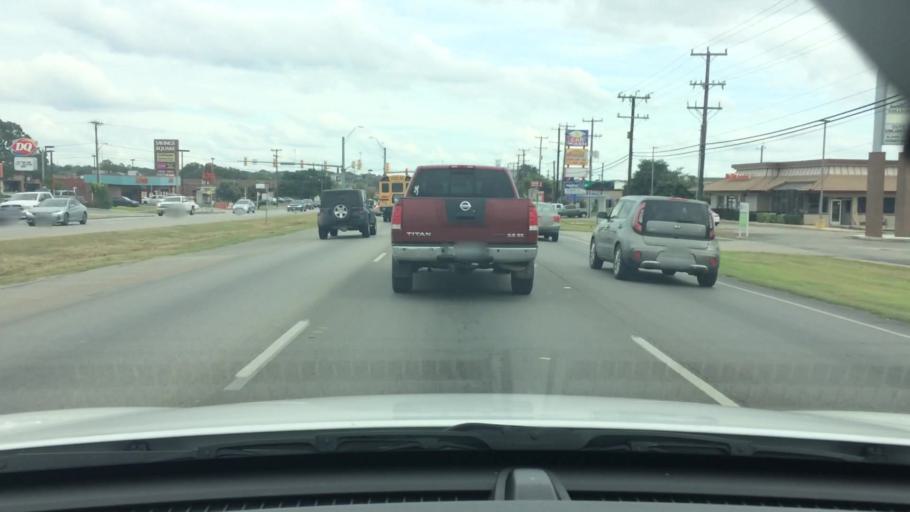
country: US
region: Texas
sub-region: Bexar County
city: Leon Valley
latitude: 29.4969
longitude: -98.6211
